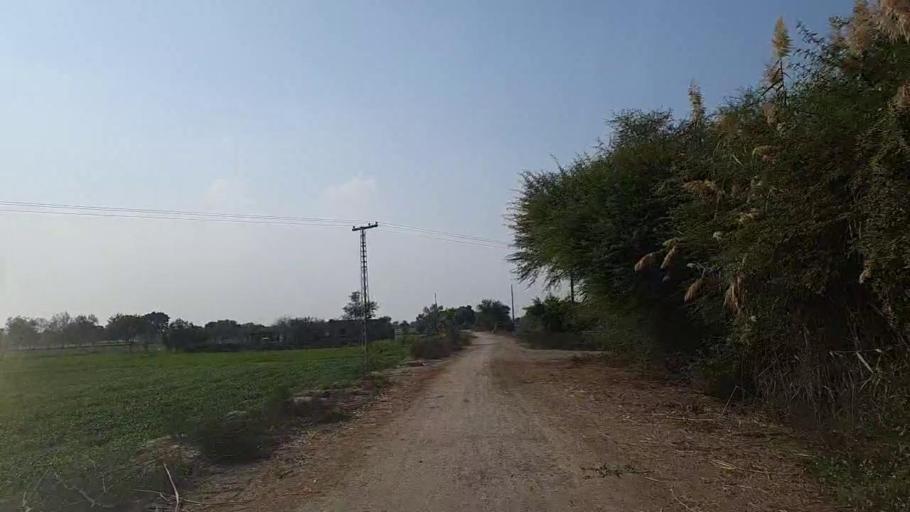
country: PK
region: Sindh
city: Jam Sahib
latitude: 26.2899
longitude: 68.5619
